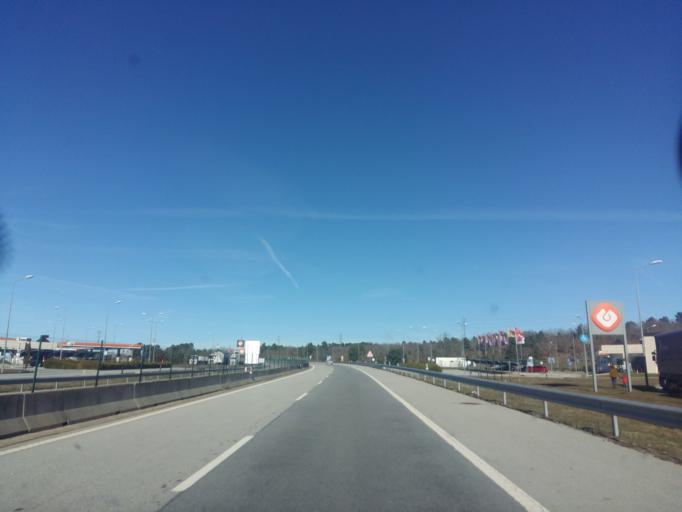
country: PT
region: Guarda
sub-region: Guarda
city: Sequeira
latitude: 40.5429
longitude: -7.2162
